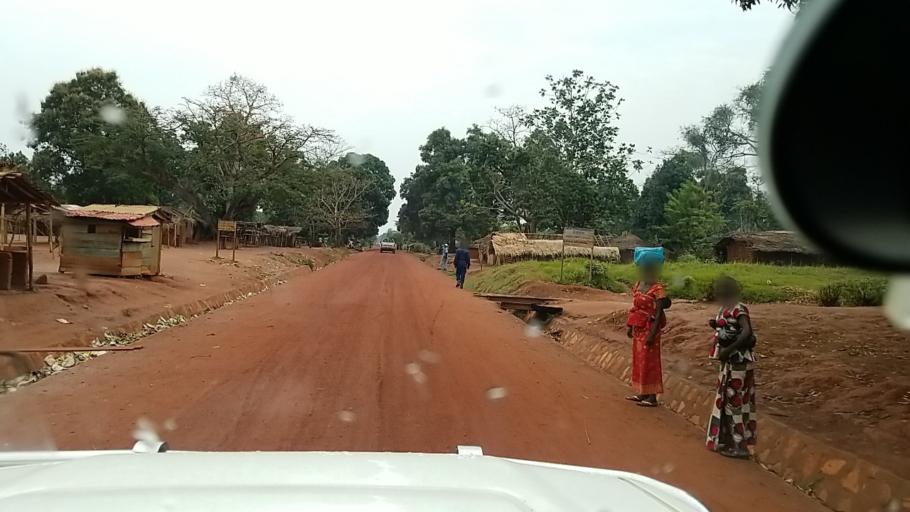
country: CD
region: Equateur
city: Gemena
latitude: 3.2203
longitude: 19.7798
